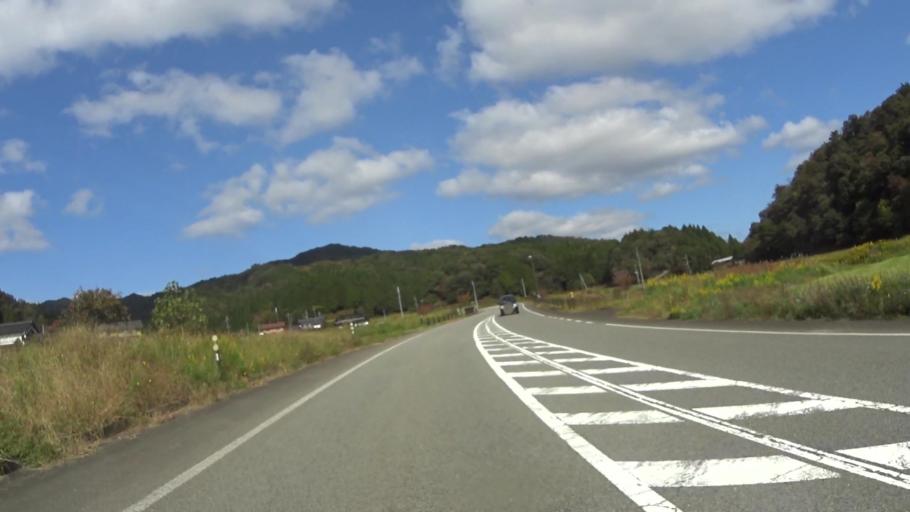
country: JP
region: Hyogo
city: Toyooka
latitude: 35.5069
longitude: 134.9913
